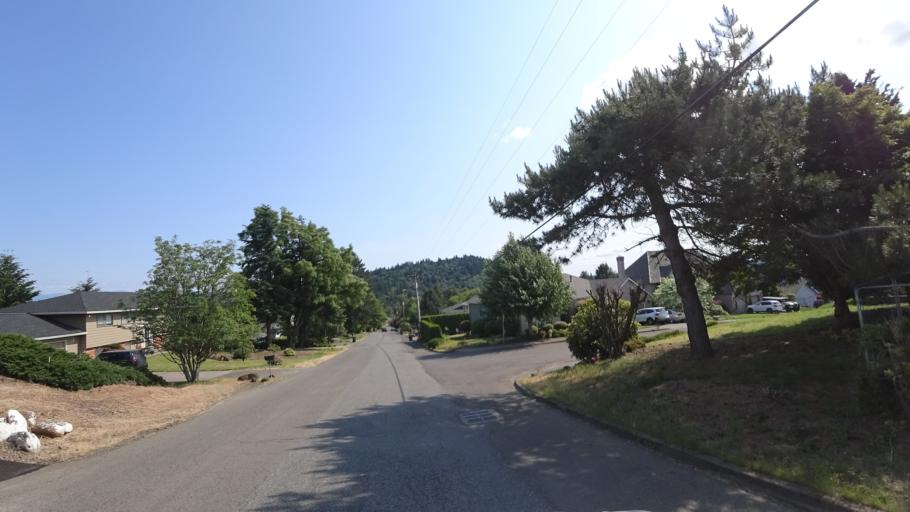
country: US
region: Oregon
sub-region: Clackamas County
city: Happy Valley
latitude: 45.4380
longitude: -122.5479
